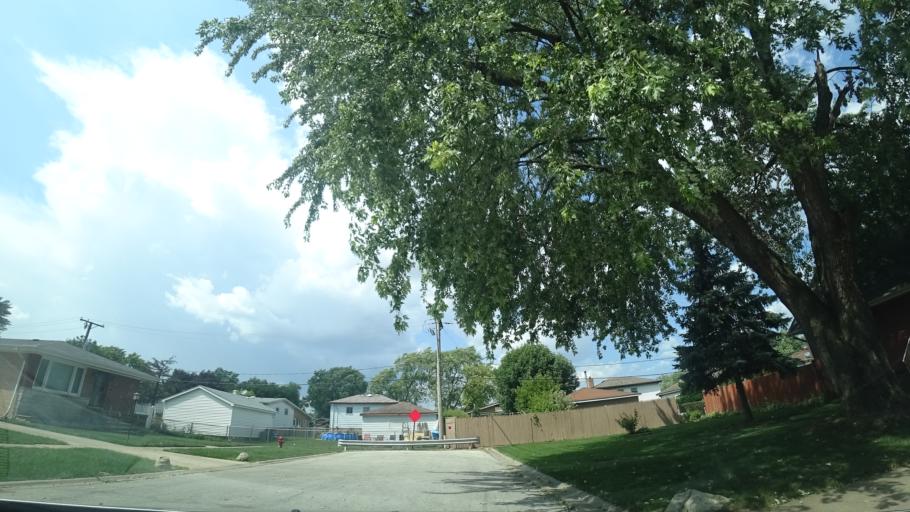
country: US
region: Illinois
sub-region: Cook County
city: Merrionette Park
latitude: 41.6713
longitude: -87.7133
